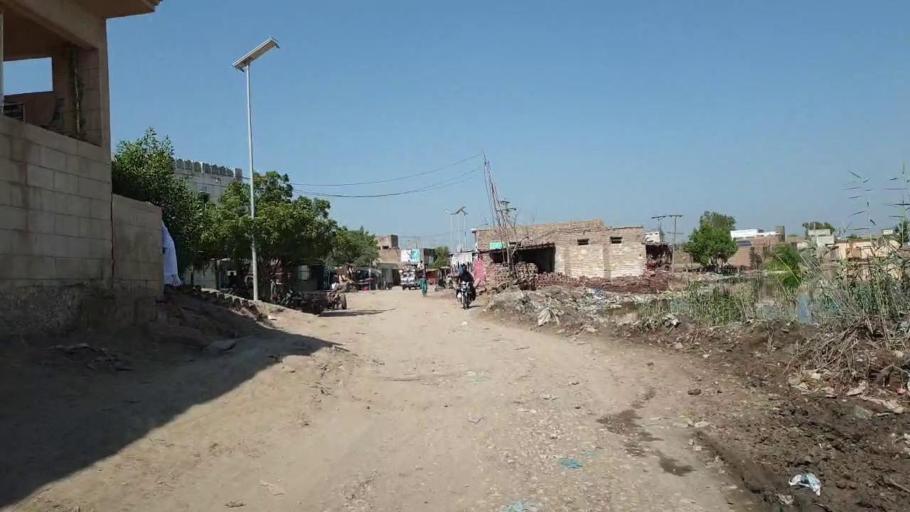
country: PK
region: Sindh
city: Matiari
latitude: 25.4997
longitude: 68.4635
